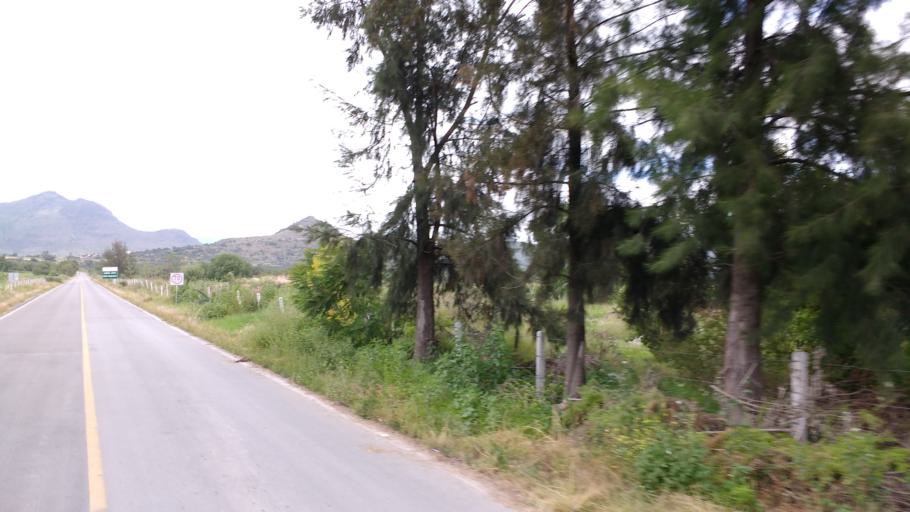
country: MX
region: Hidalgo
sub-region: Tezontepec de Aldama
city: Tenango
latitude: 20.2277
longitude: -99.2592
